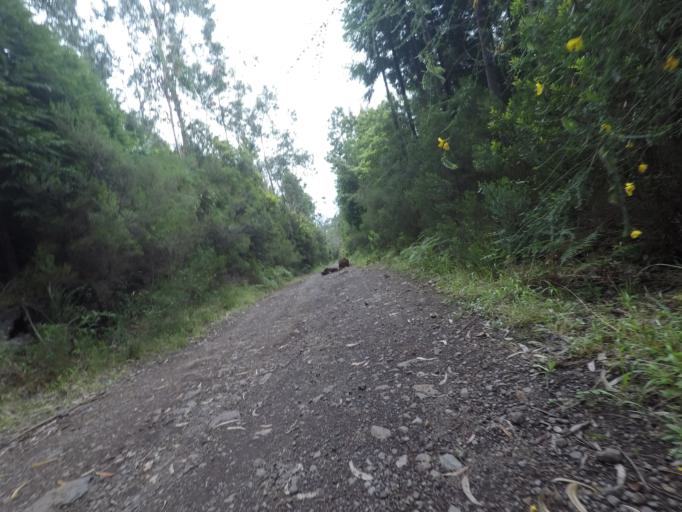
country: PT
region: Madeira
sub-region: Sao Vicente
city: Sao Vicente
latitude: 32.7746
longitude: -17.0479
